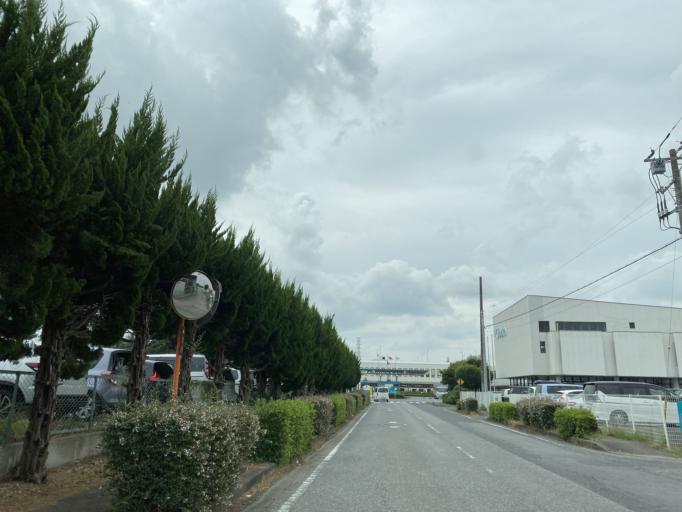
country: JP
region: Ibaraki
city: Mitsukaido
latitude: 36.0269
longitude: 140.0460
